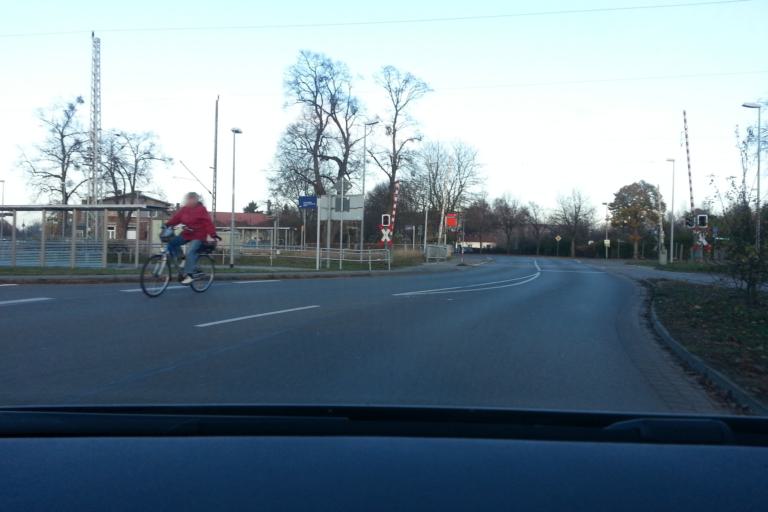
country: DE
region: Mecklenburg-Vorpommern
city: Ferdinandshof
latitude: 53.6583
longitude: 13.8827
